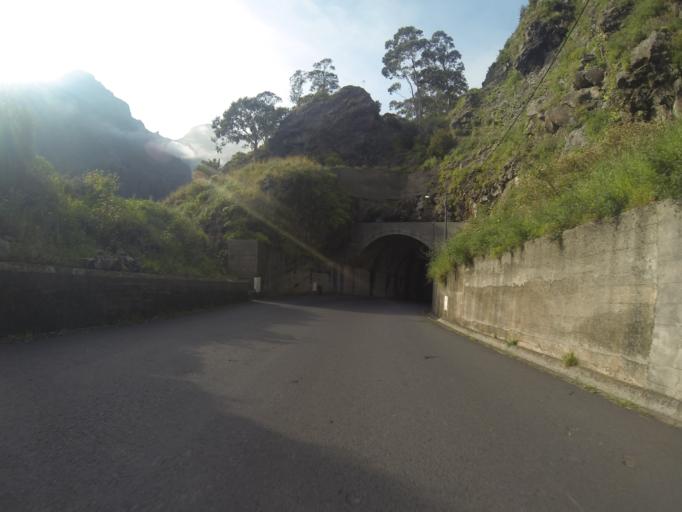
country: PT
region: Madeira
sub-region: Camara de Lobos
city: Curral das Freiras
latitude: 32.7275
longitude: -16.9657
